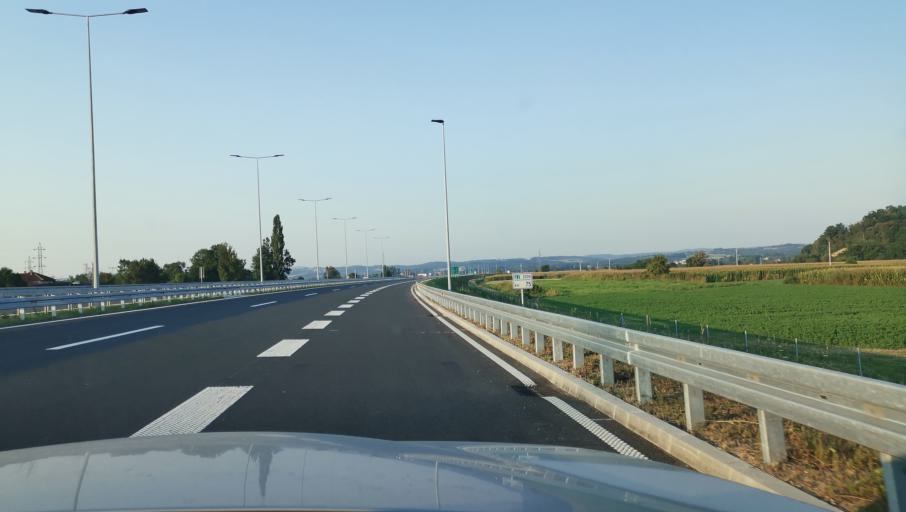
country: RS
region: Central Serbia
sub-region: Kolubarski Okrug
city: Ljig
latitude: 44.2359
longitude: 20.2563
